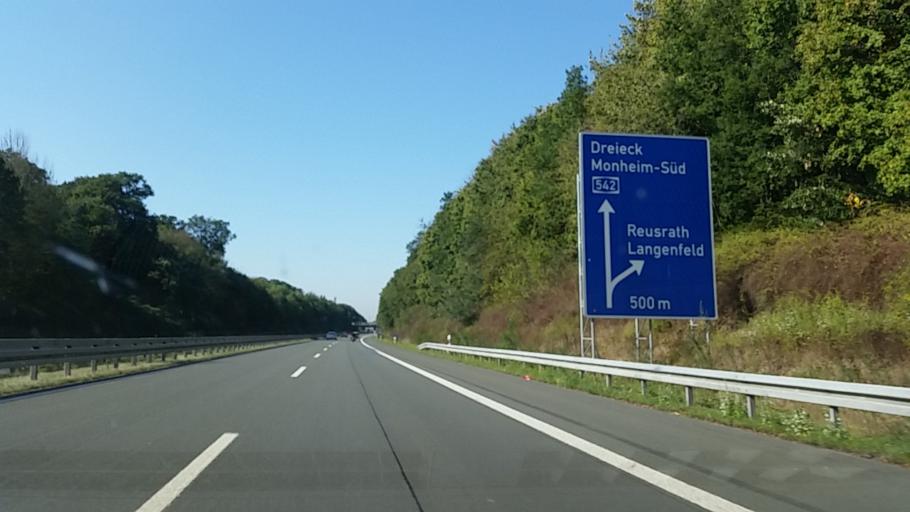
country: DE
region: North Rhine-Westphalia
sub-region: Regierungsbezirk Dusseldorf
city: Langenfeld
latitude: 51.0990
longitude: 6.9614
